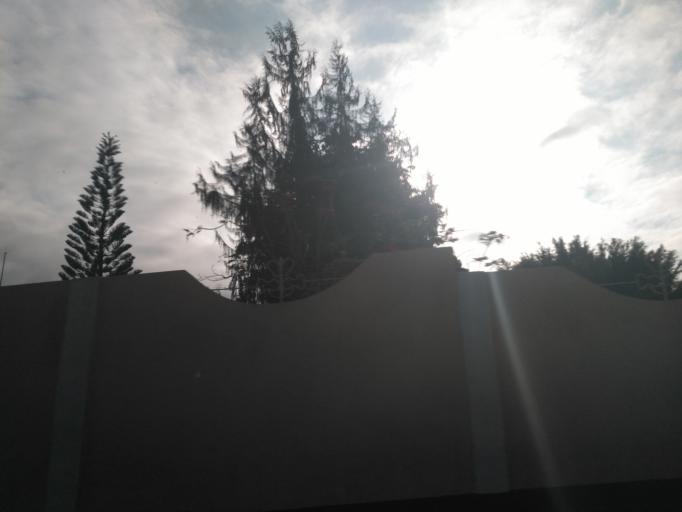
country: TZ
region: Arusha
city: Arusha
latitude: -3.3717
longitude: 36.6894
